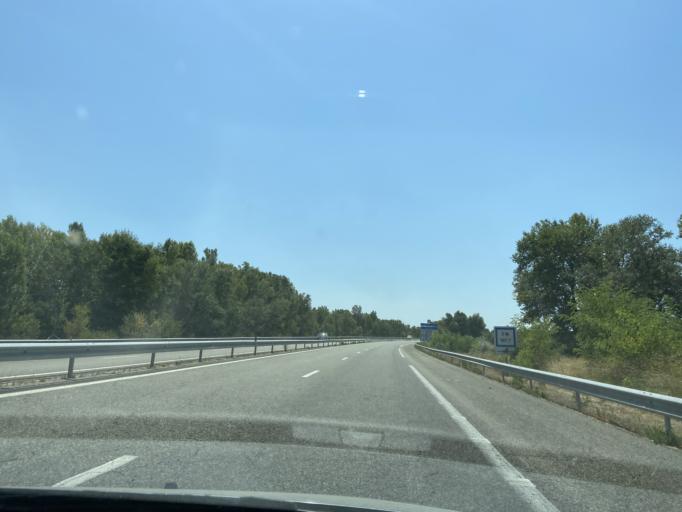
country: FR
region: Provence-Alpes-Cote d'Azur
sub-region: Departement des Alpes-de-Haute-Provence
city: Volx
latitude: 43.8553
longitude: 5.8607
